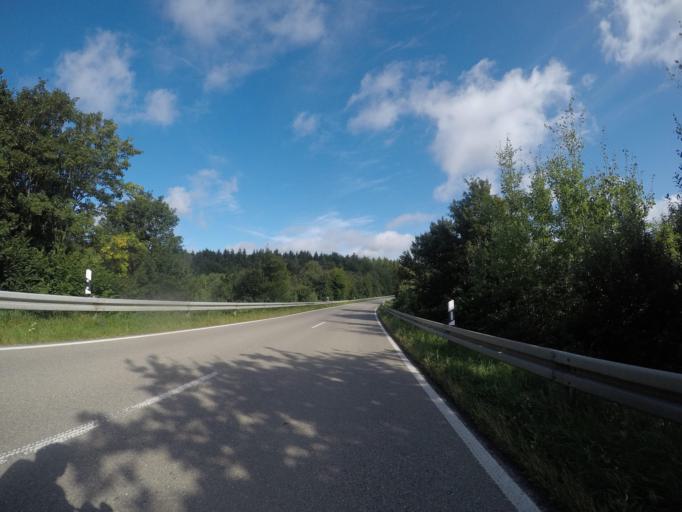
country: DE
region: Baden-Wuerttemberg
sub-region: Tuebingen Region
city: Laichingen
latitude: 48.4113
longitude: 9.6498
